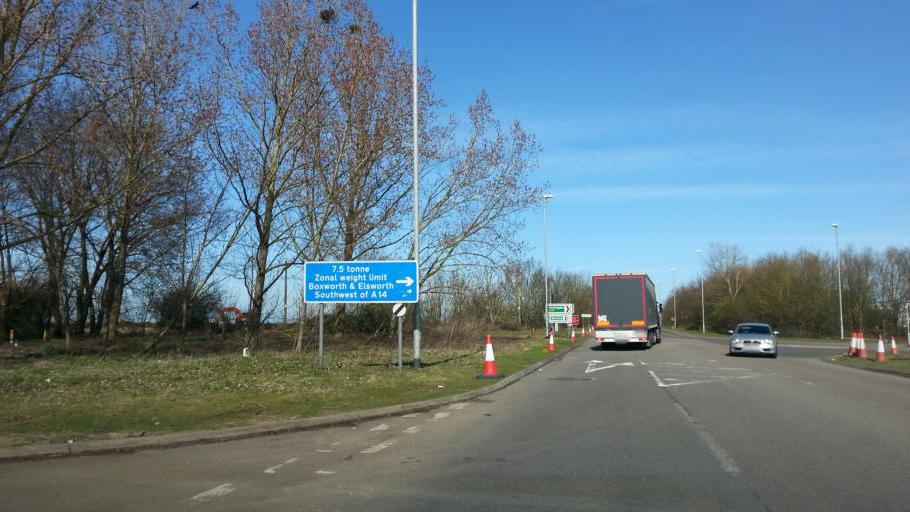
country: GB
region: England
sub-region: Cambridgeshire
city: Swavesey
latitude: 52.2738
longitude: -0.0126
